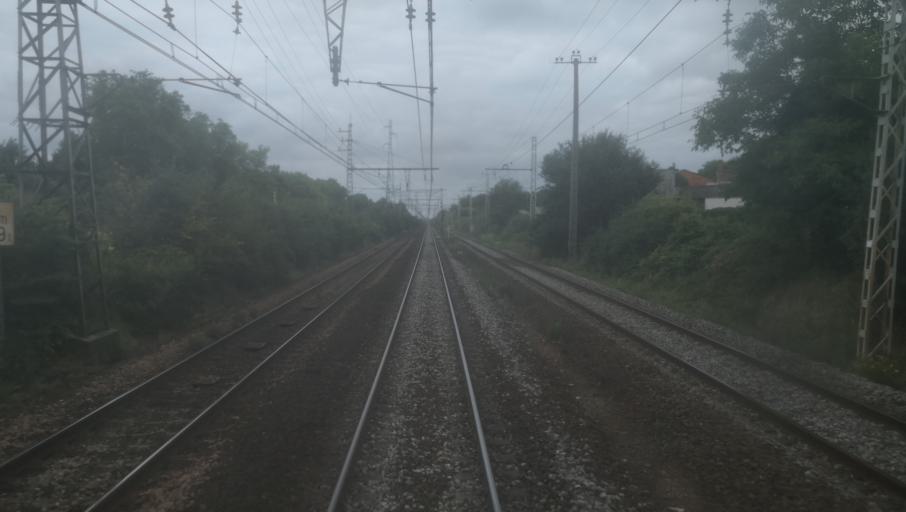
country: FR
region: Midi-Pyrenees
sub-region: Departement de la Haute-Garonne
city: Aucamville
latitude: 43.6686
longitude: 1.4103
